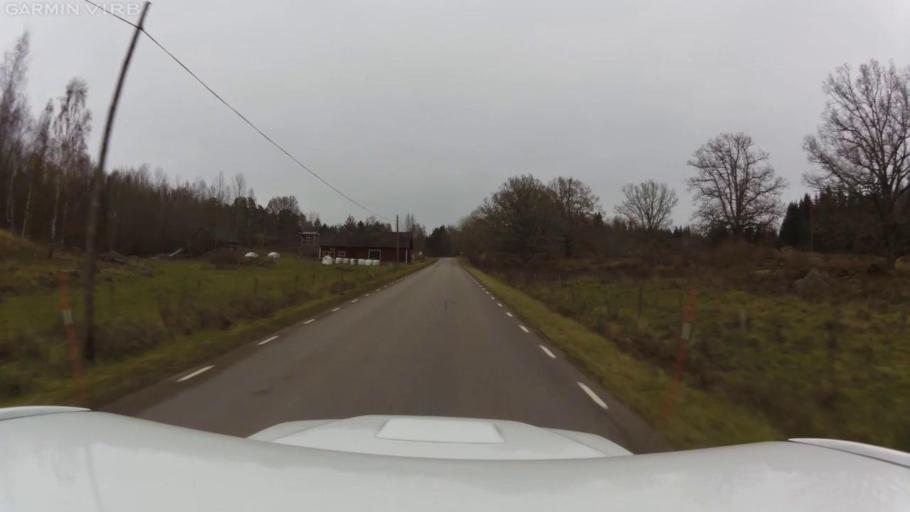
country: SE
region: OEstergoetland
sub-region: Linkopings Kommun
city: Vikingstad
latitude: 58.2541
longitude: 15.3837
